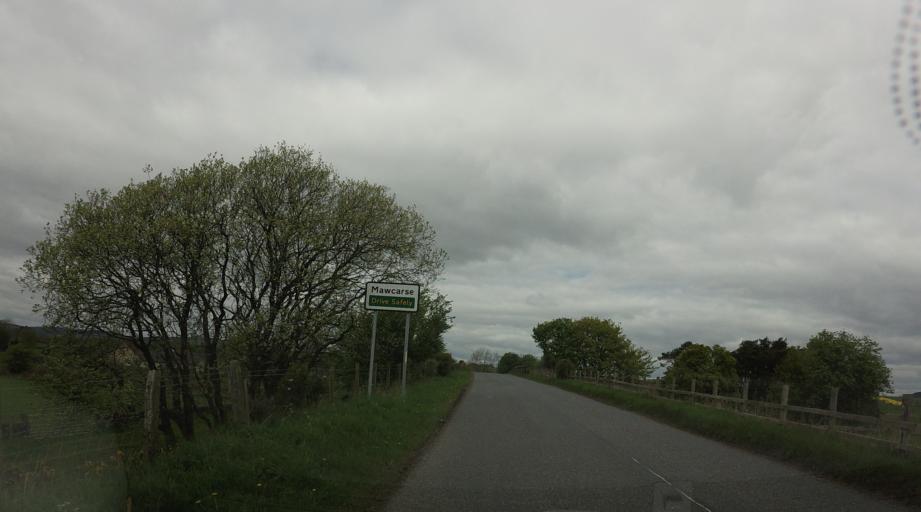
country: GB
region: Scotland
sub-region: Perth and Kinross
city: Milnathort
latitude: 56.2390
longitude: -3.3672
